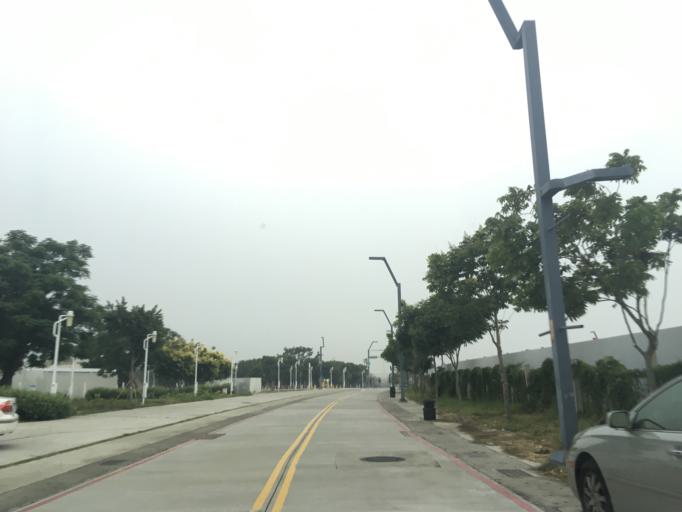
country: TW
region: Taiwan
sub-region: Taichung City
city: Taichung
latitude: 24.1921
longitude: 120.6519
